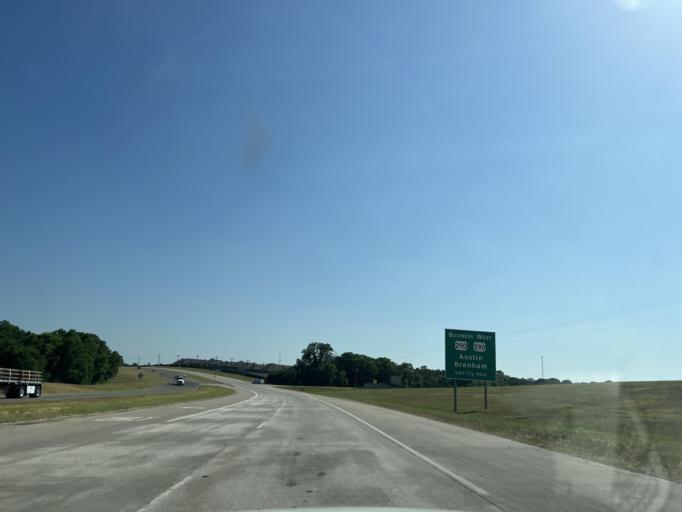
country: US
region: Texas
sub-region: Washington County
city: Brenham
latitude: 30.1765
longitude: -96.4232
